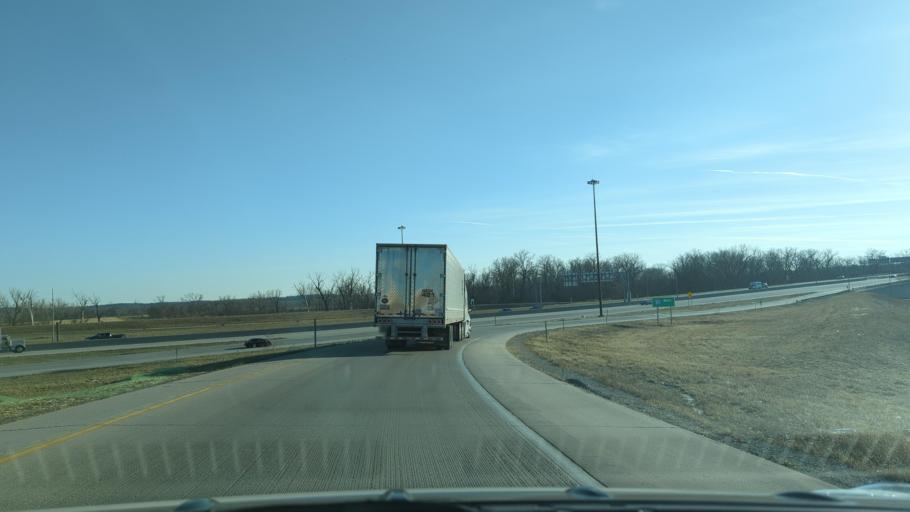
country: US
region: Nebraska
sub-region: Douglas County
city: Omaha
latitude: 41.2340
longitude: -95.9010
